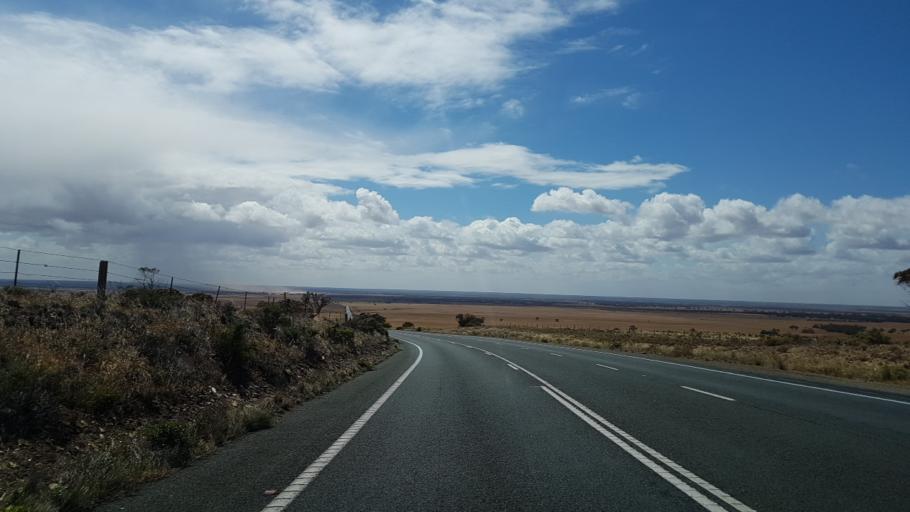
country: AU
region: South Australia
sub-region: Barossa
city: Angaston
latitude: -34.4034
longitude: 139.2289
